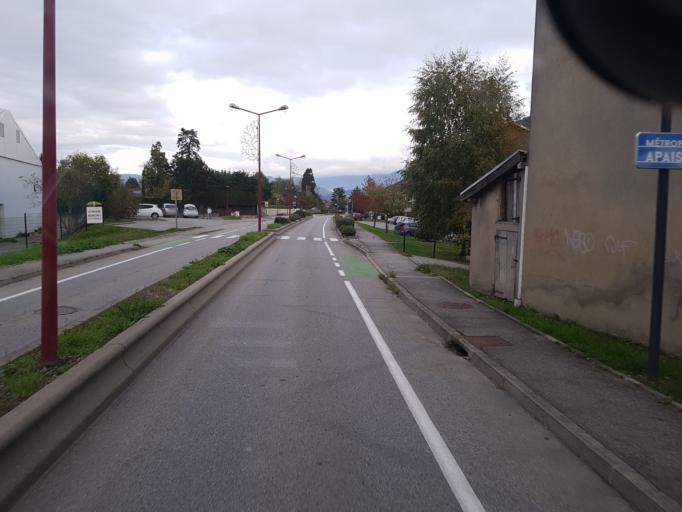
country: FR
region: Rhone-Alpes
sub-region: Departement de l'Isere
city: Vif
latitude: 45.0514
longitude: 5.6736
